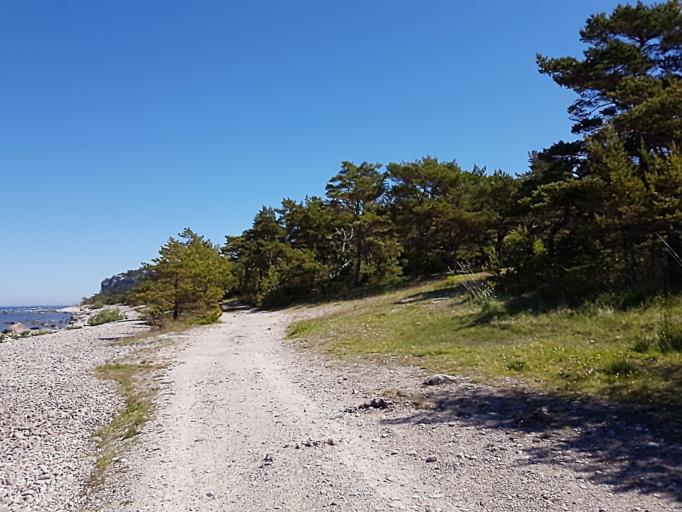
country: SE
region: Gotland
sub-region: Gotland
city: Slite
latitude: 57.8318
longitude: 18.5327
